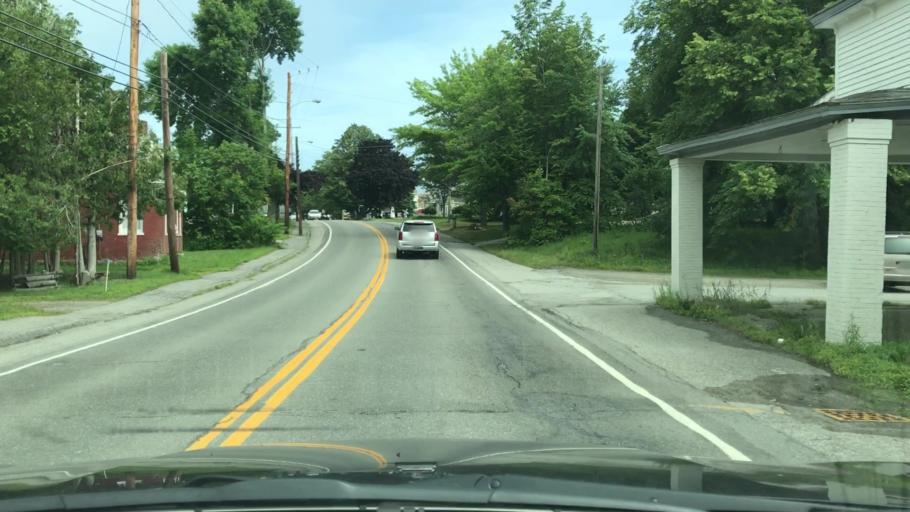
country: US
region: Maine
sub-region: Waldo County
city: Stockton Springs
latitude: 44.4582
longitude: -68.9202
